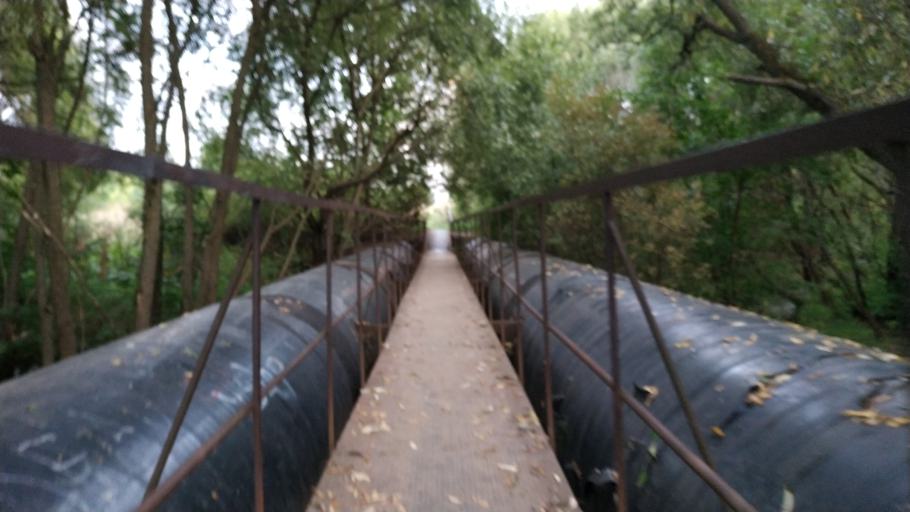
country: RU
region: Moscow
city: Solntsevo
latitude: 55.6412
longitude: 37.3747
